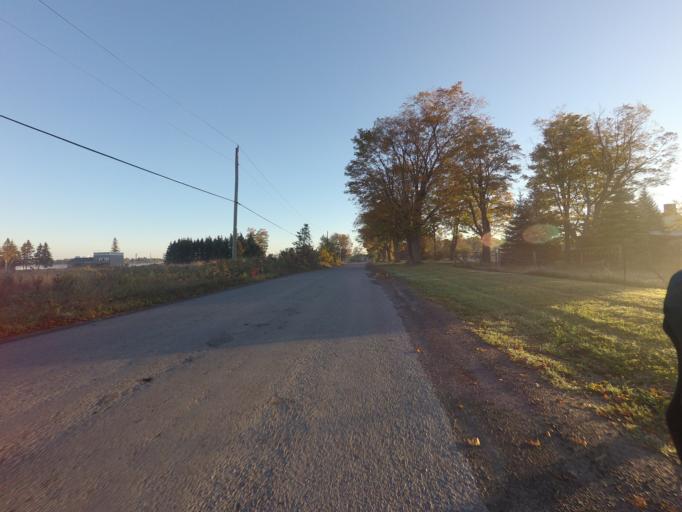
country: CA
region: Ontario
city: Quinte West
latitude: 44.0367
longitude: -77.5938
